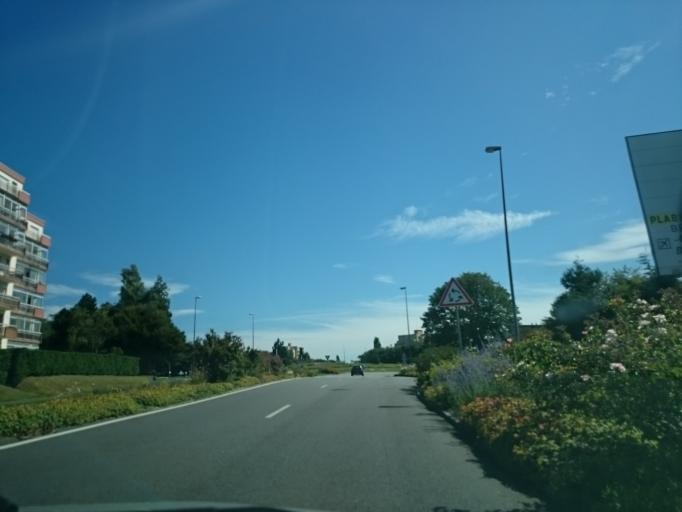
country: FR
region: Brittany
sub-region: Departement du Finistere
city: Brest
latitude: 48.4140
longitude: -4.4816
